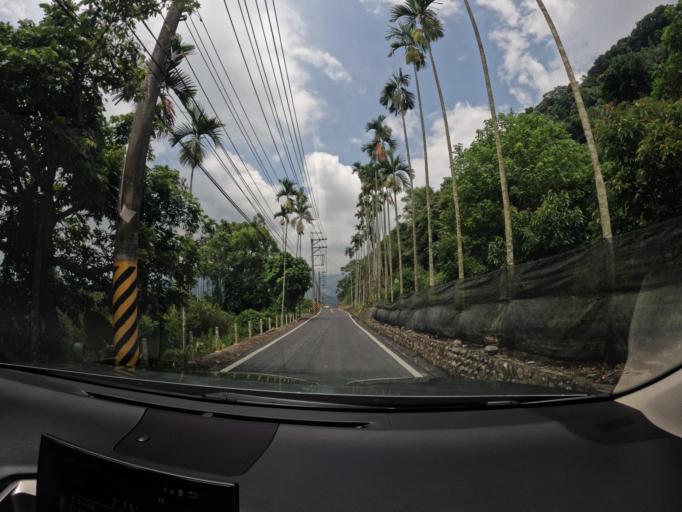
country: TW
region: Taiwan
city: Lugu
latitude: 23.8075
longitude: 120.7982
